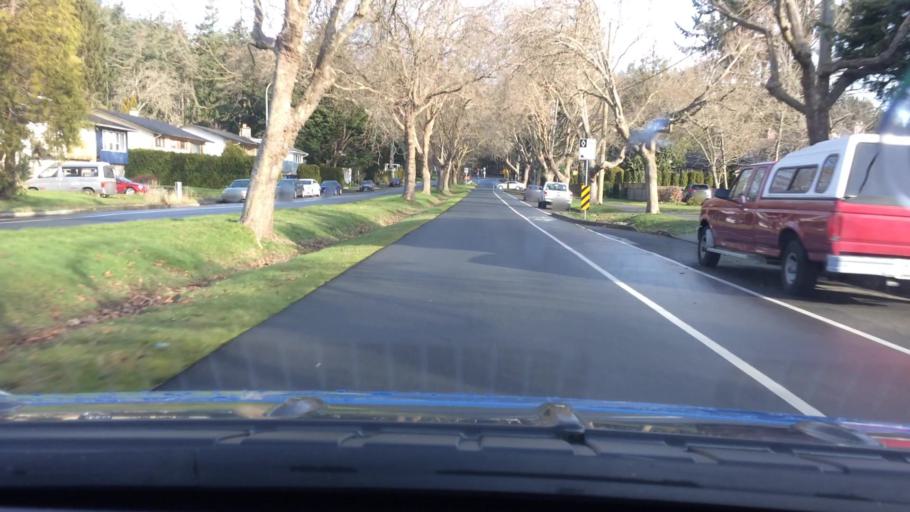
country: CA
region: British Columbia
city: Oak Bay
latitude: 48.4879
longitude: -123.3376
